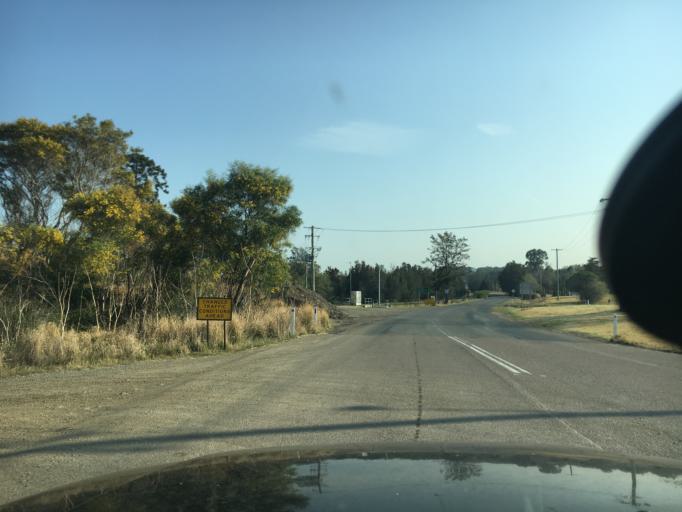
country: AU
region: New South Wales
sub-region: Cessnock
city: Branxton
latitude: -32.6560
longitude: 151.3572
